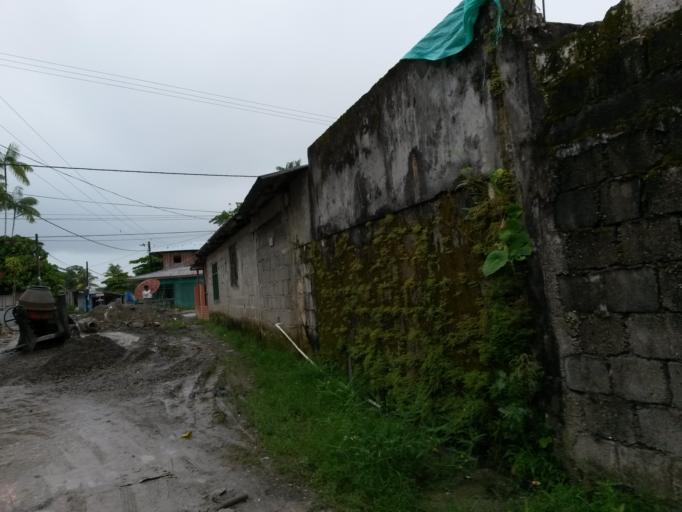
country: CO
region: Cauca
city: Guapi
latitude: 2.5731
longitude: -77.8882
